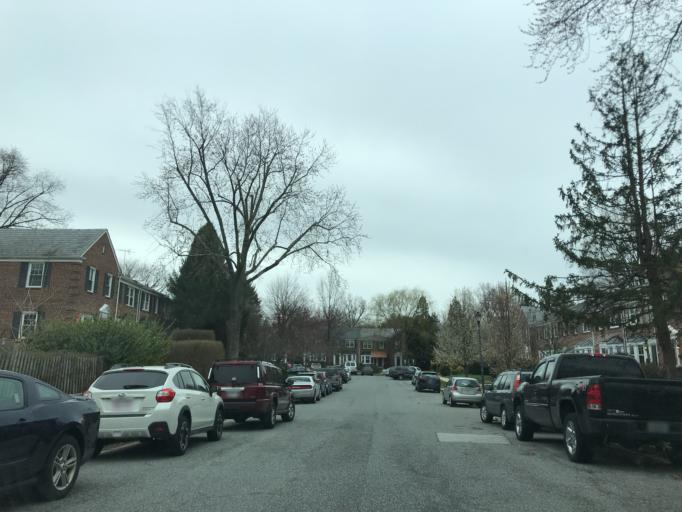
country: US
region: Maryland
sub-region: Baltimore County
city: Towson
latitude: 39.3827
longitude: -76.6088
